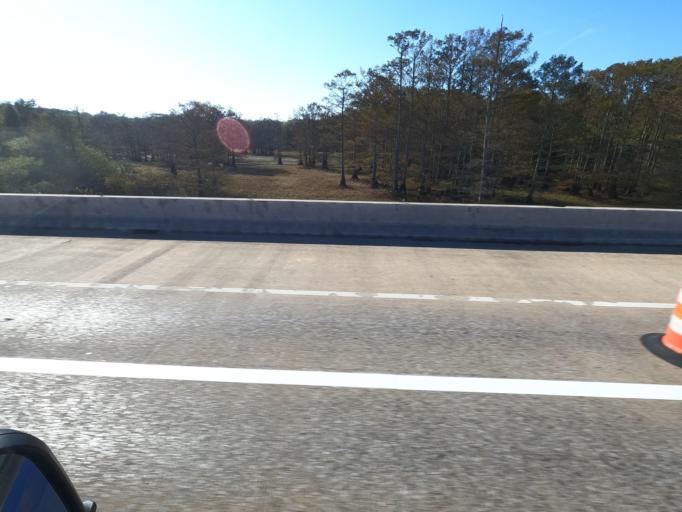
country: US
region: Tennessee
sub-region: Dyer County
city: Dyersburg
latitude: 35.9972
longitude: -89.3421
